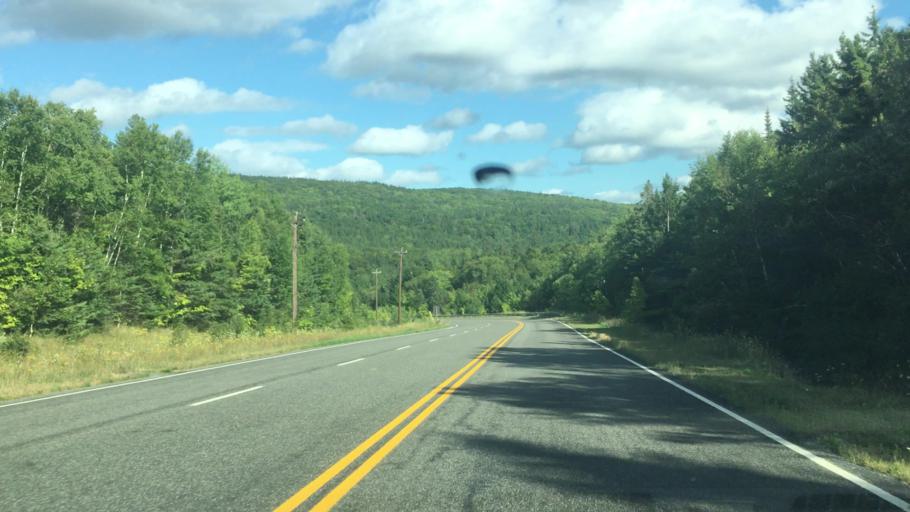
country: CA
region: Nova Scotia
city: Sydney
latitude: 45.8135
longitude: -60.6768
